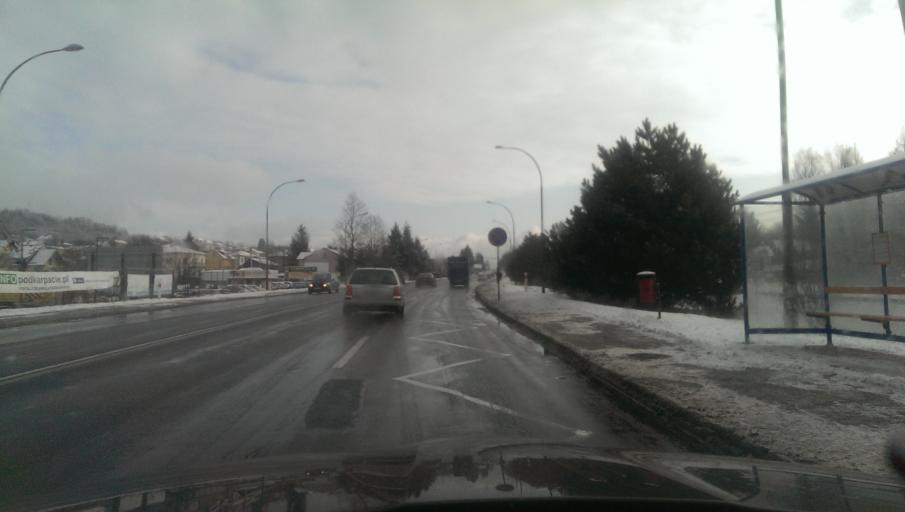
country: PL
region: Subcarpathian Voivodeship
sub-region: Powiat sanocki
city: Sanok
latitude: 49.5691
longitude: 22.1651
